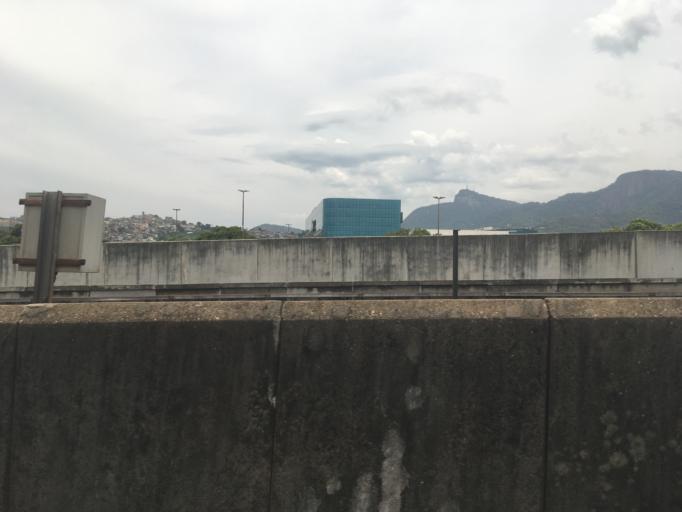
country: BR
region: Rio de Janeiro
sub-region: Rio De Janeiro
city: Rio de Janeiro
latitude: -22.9095
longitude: -43.2088
